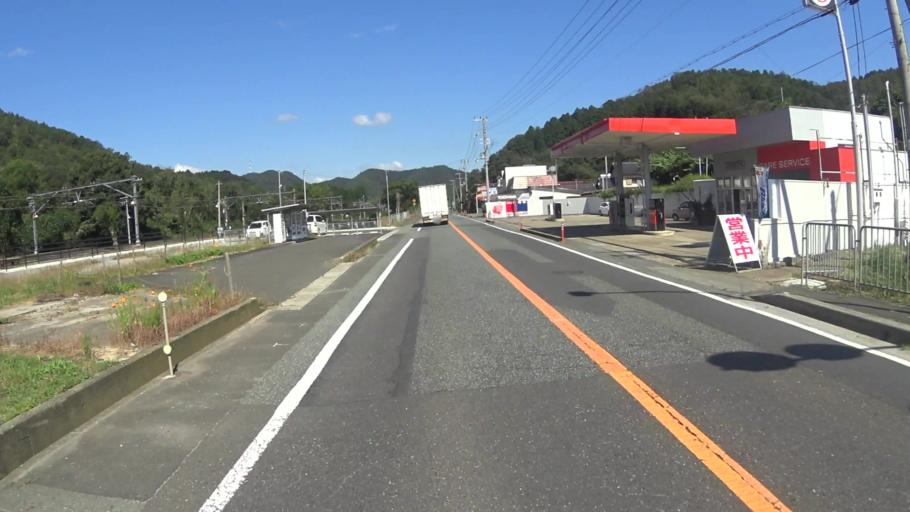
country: JP
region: Kyoto
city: Ayabe
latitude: 35.3487
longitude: 135.3116
